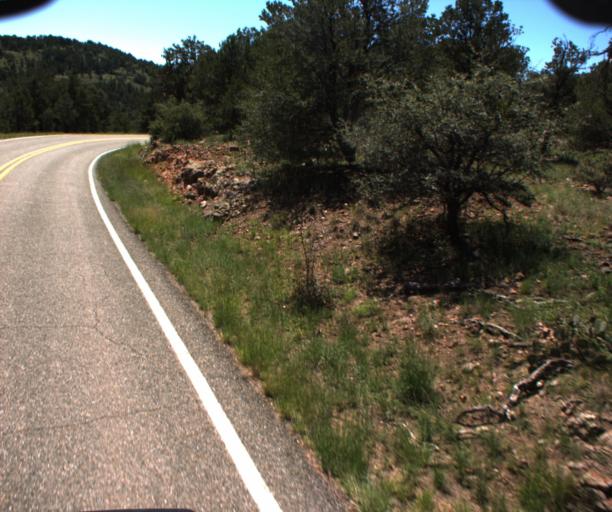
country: US
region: Arizona
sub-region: Greenlee County
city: Morenci
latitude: 33.3595
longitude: -109.3422
